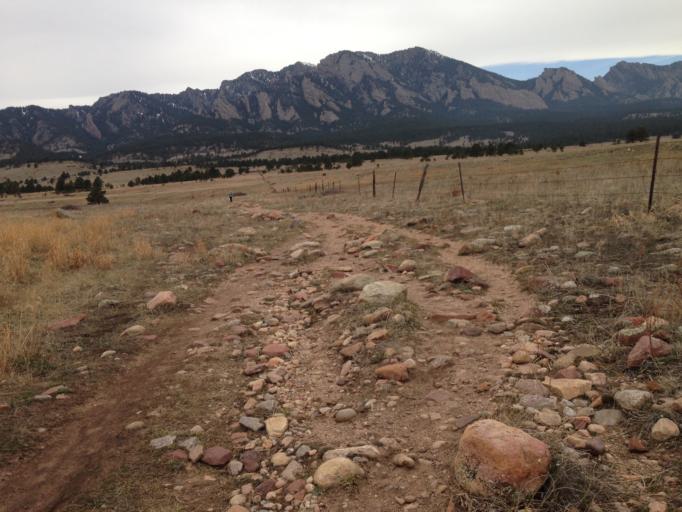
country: US
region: Colorado
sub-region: Boulder County
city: Boulder
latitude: 39.9502
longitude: -105.2468
